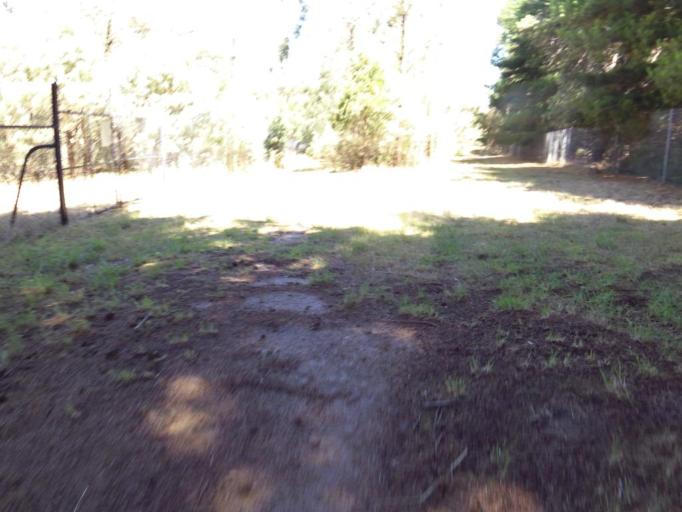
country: AU
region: Victoria
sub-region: Hume
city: Sunbury
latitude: -37.3555
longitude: 144.5493
